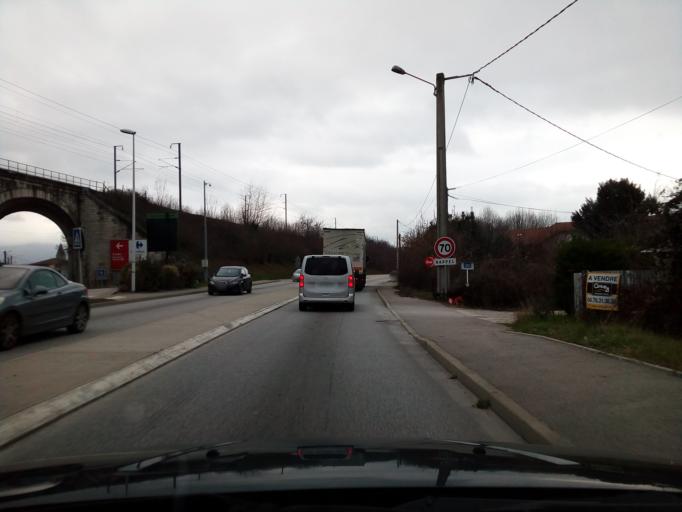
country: FR
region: Rhone-Alpes
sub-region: Departement de l'Isere
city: Saint-Jean-de-Moirans
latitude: 45.3271
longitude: 5.5737
